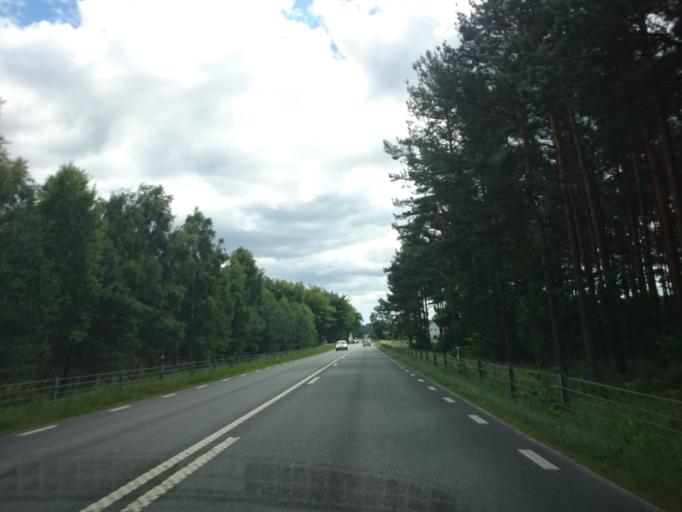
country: SE
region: Skane
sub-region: Kristianstads Kommun
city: Degeberga
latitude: 55.8159
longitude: 14.1312
